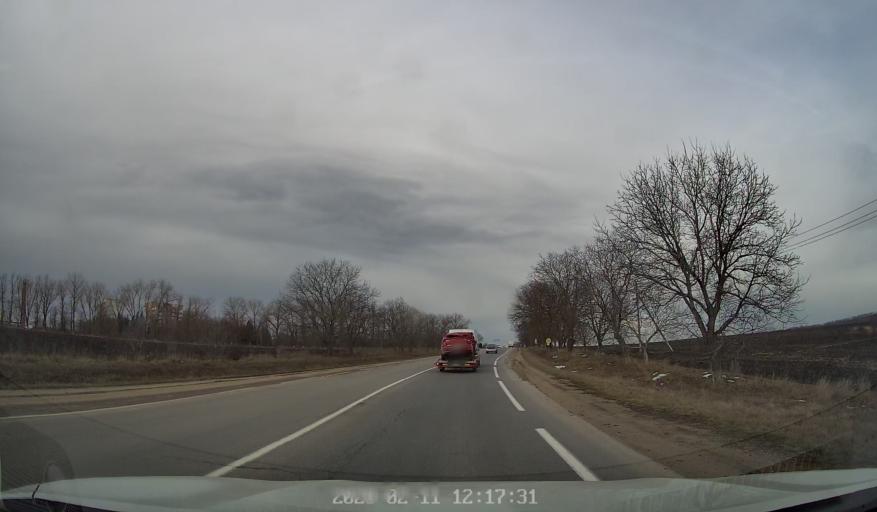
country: MD
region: Raionul Edinet
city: Edinet
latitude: 48.0996
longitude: 27.4152
